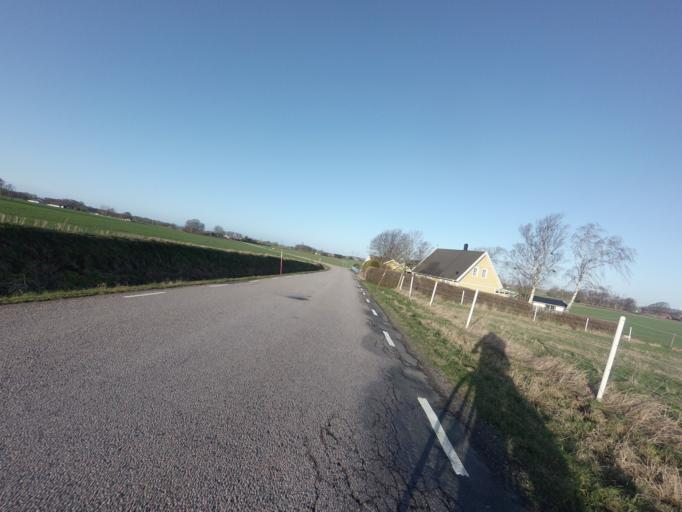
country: SE
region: Skane
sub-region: Hoganas Kommun
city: Hoganas
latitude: 56.1357
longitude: 12.6374
